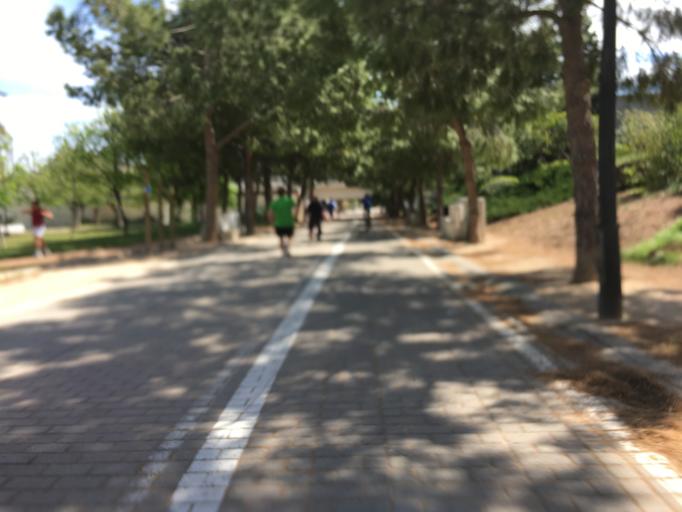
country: ES
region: Valencia
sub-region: Provincia de Valencia
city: Valencia
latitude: 39.4749
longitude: -0.3970
